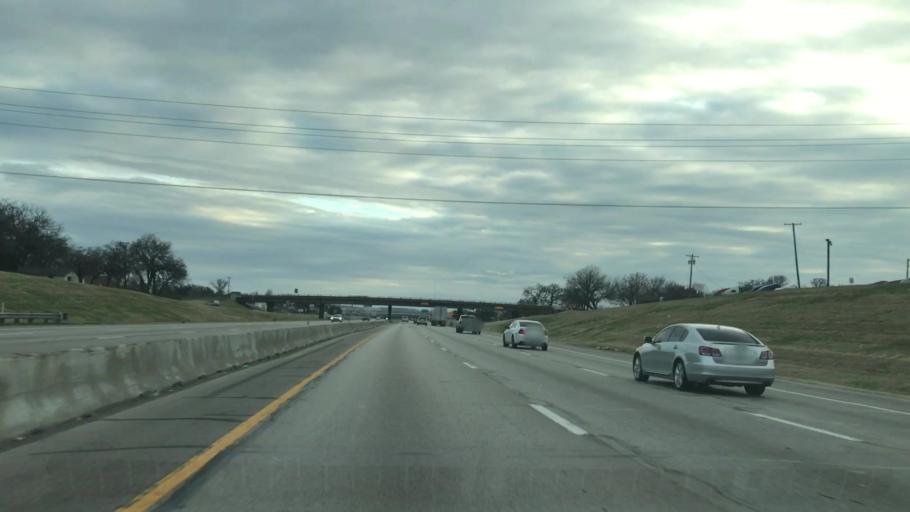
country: US
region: Texas
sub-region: Dallas County
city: Irving
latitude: 32.8087
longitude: -96.9217
